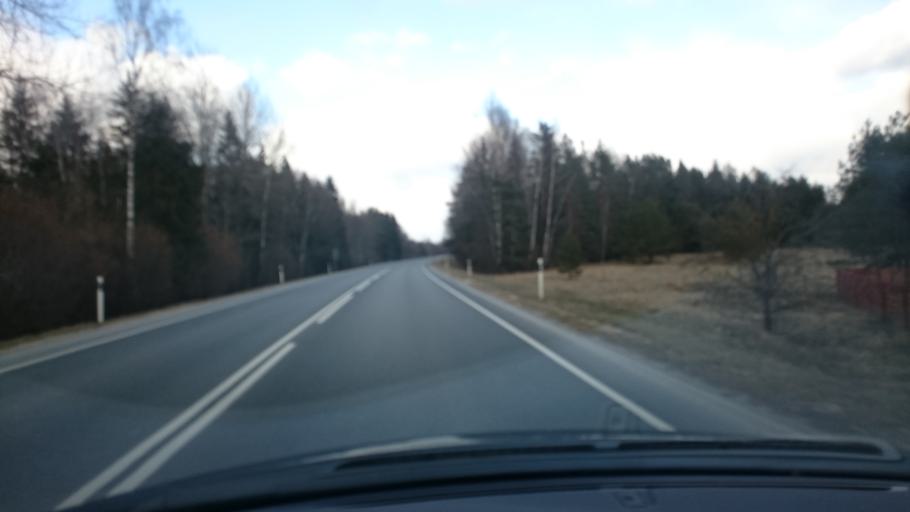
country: EE
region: Harju
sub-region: Nissi vald
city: Riisipere
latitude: 59.1136
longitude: 24.2624
